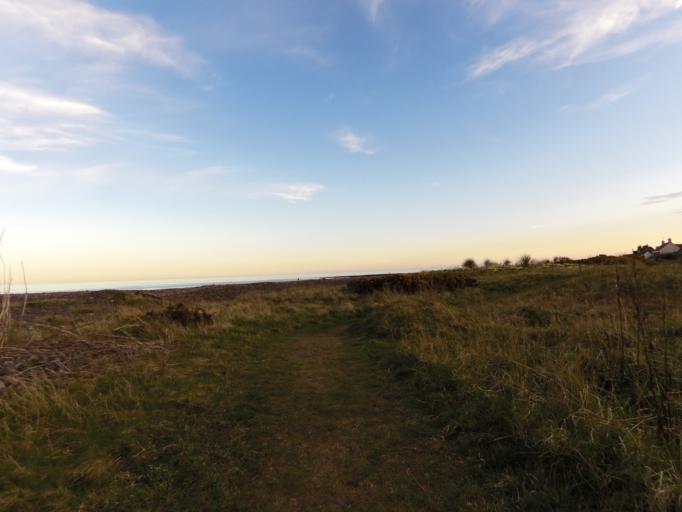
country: GB
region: Scotland
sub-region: Aberdeenshire
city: Inverbervie
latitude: 56.8111
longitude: -2.3060
